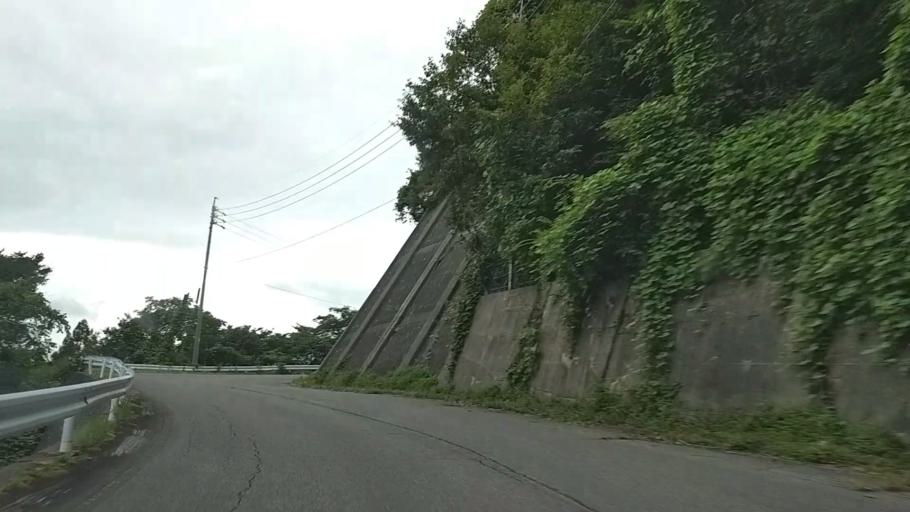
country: JP
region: Nagano
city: Iiyama
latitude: 36.8157
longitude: 138.3728
